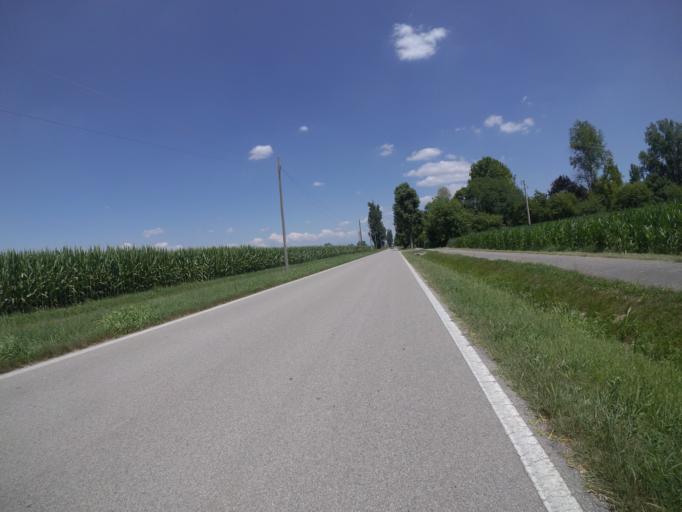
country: IT
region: Friuli Venezia Giulia
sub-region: Provincia di Udine
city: Varmo
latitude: 45.9234
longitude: 12.9980
